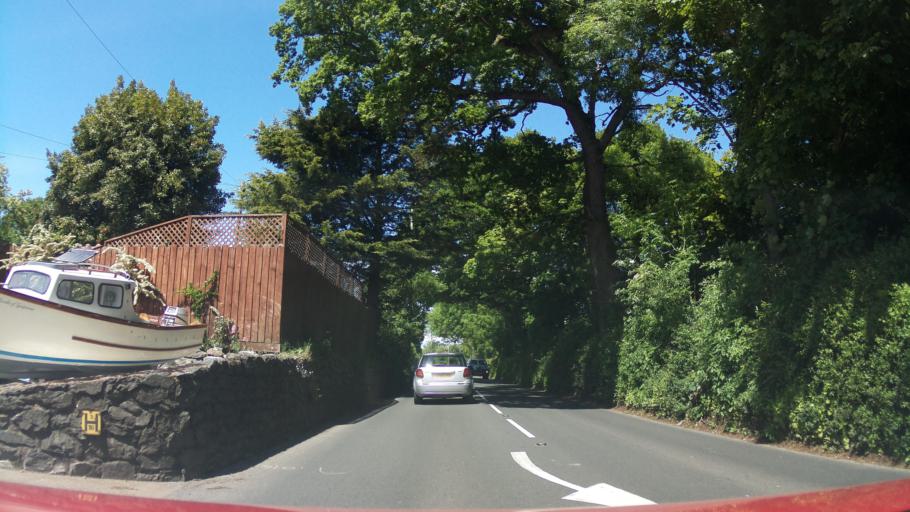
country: GB
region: England
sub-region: Devon
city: Exmouth
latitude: 50.6488
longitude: -3.4170
